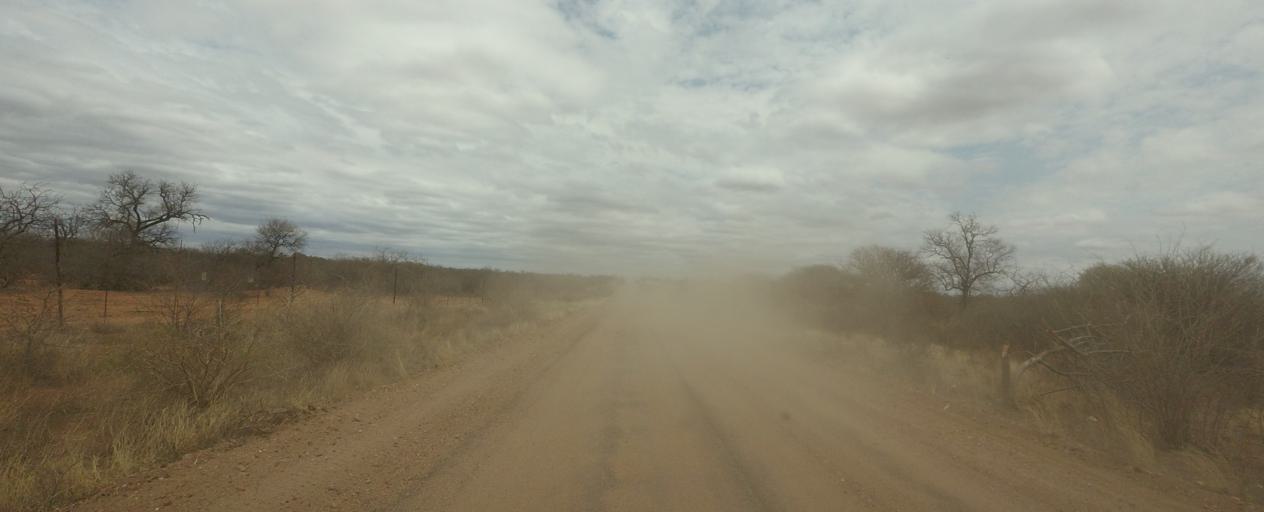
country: BW
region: Central
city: Mathathane
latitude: -22.6752
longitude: 28.6728
